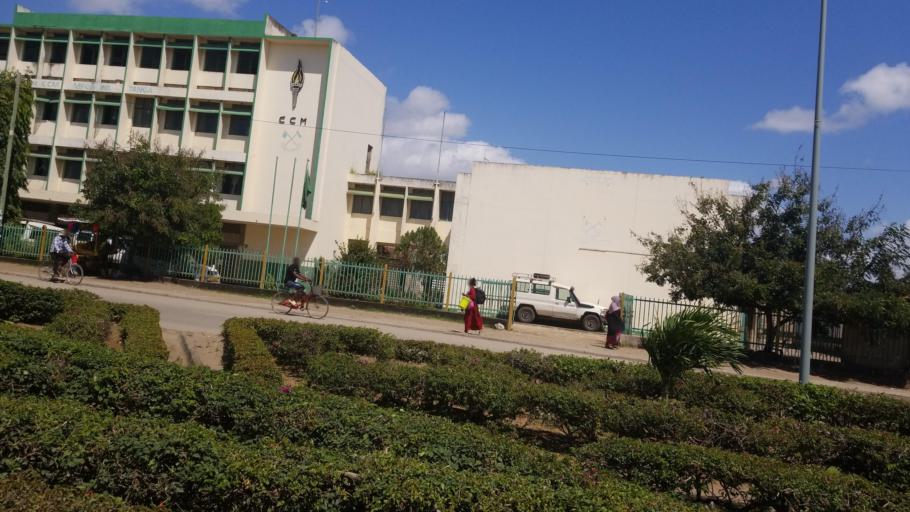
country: TZ
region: Tanga
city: Tanga
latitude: -5.0840
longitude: 39.0975
